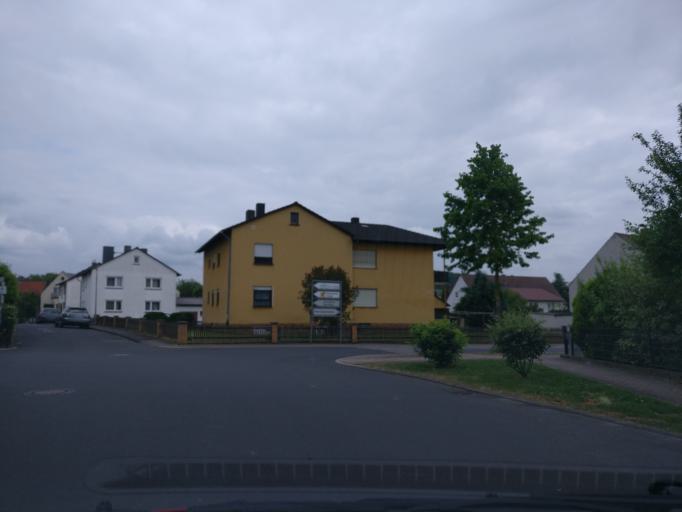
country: DE
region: Hesse
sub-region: Regierungsbezirk Kassel
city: Kassel
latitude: 51.3512
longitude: 9.5292
